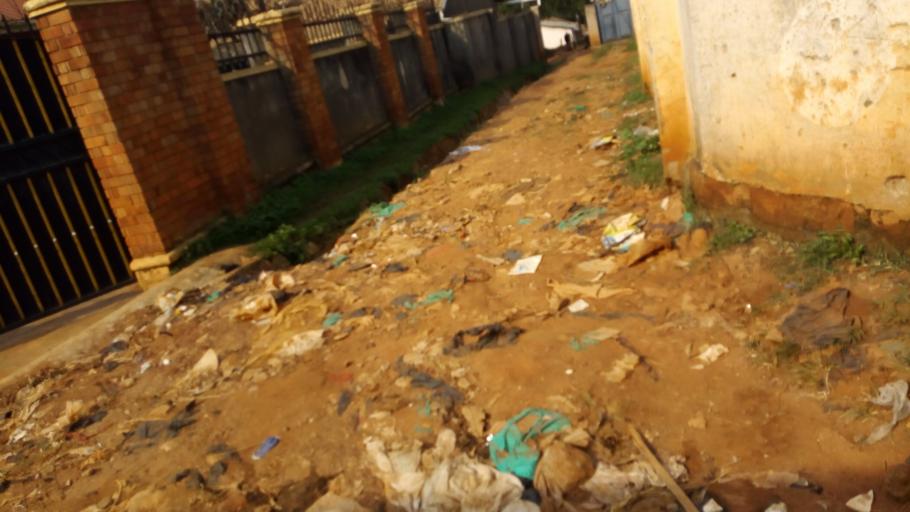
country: UG
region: Central Region
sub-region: Wakiso District
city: Kireka
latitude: 0.3114
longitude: 32.6507
